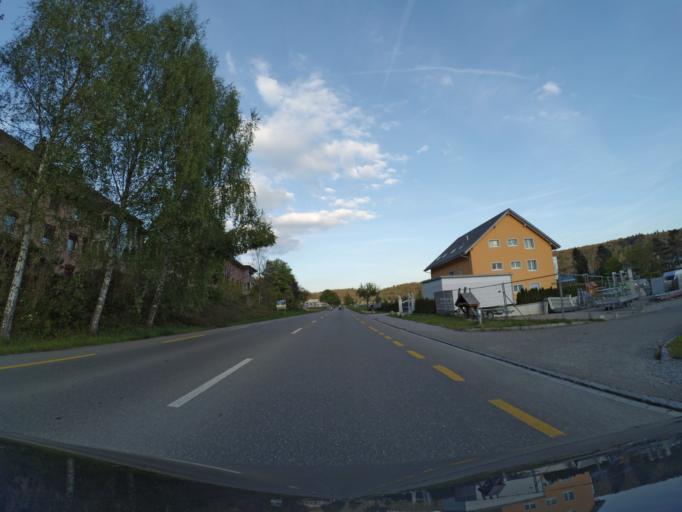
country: CH
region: Schaffhausen
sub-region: Bezirk Schaffhausen
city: Beringen
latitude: 47.6964
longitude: 8.5860
